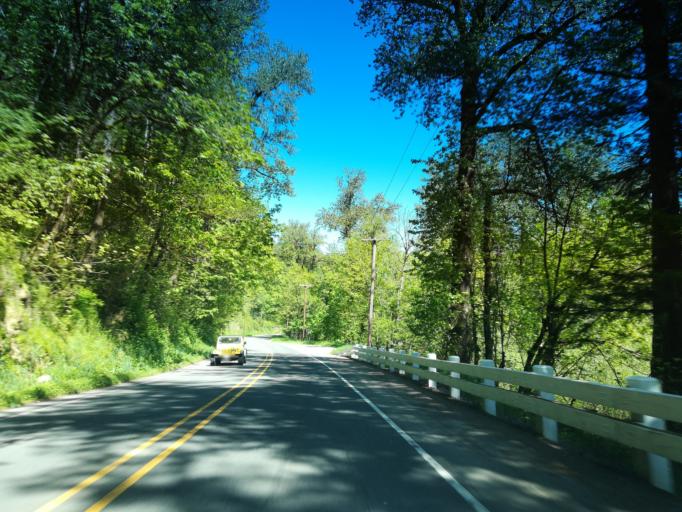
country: US
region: Oregon
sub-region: Multnomah County
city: Troutdale
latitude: 45.5168
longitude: -122.3593
